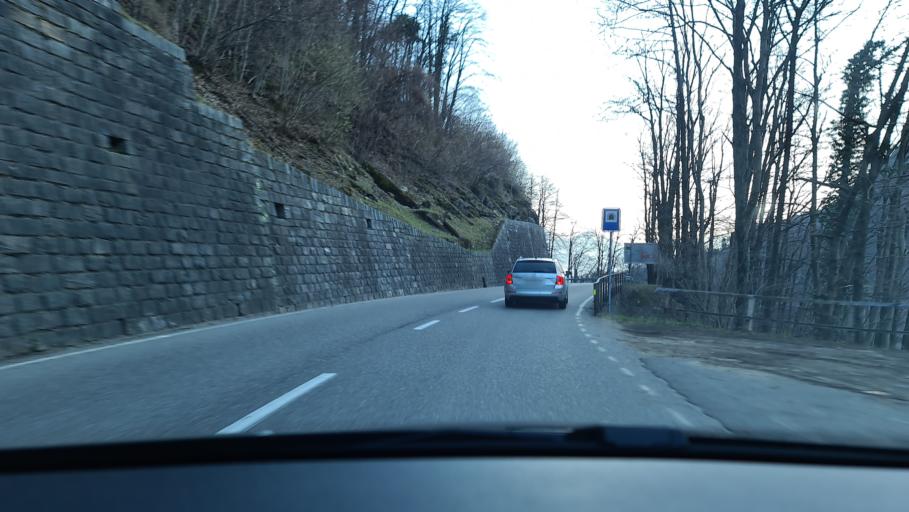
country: CH
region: Ticino
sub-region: Locarno District
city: Gordola
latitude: 46.1973
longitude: 8.8516
